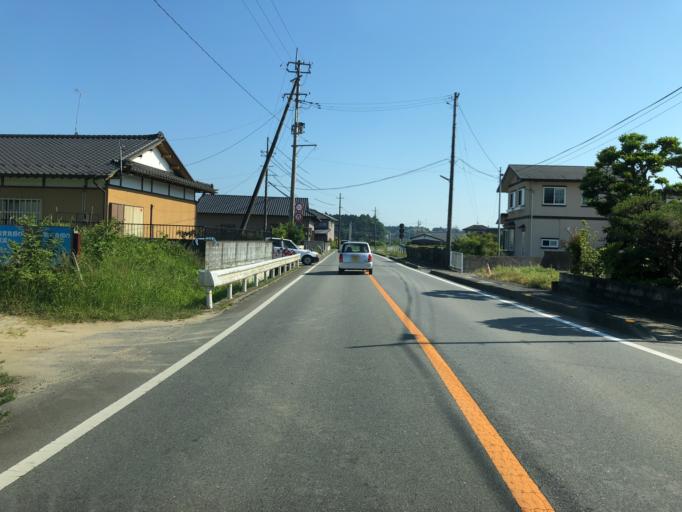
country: JP
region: Fukushima
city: Iwaki
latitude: 36.9348
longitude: 140.7980
